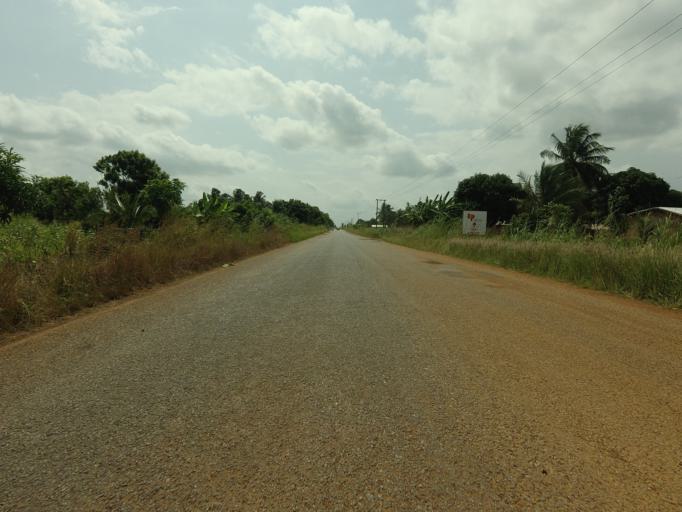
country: TG
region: Maritime
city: Lome
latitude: 6.1861
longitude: 1.0645
